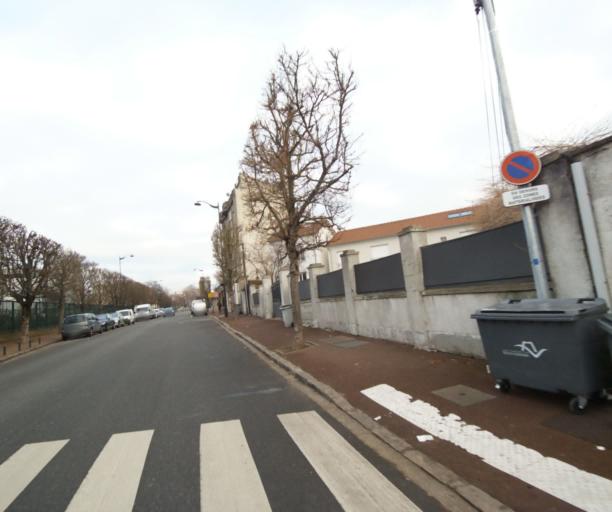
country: FR
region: Ile-de-France
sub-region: Departement des Hauts-de-Seine
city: Rueil-Malmaison
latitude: 48.8693
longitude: 2.2036
